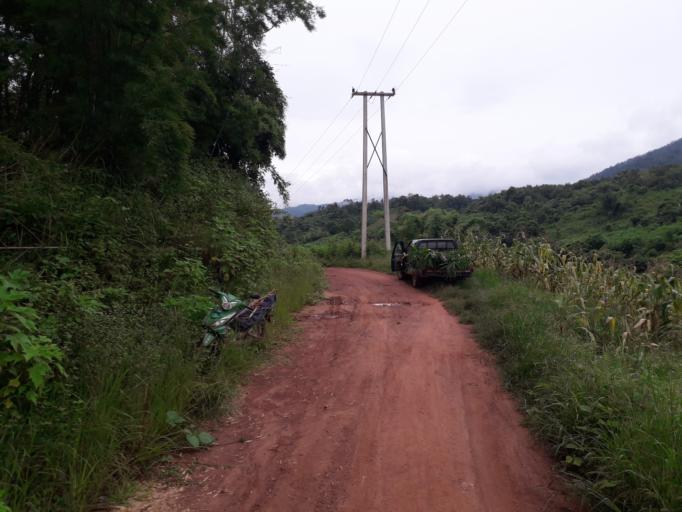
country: CN
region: Yunnan
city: Menglie
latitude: 22.2431
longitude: 101.6097
